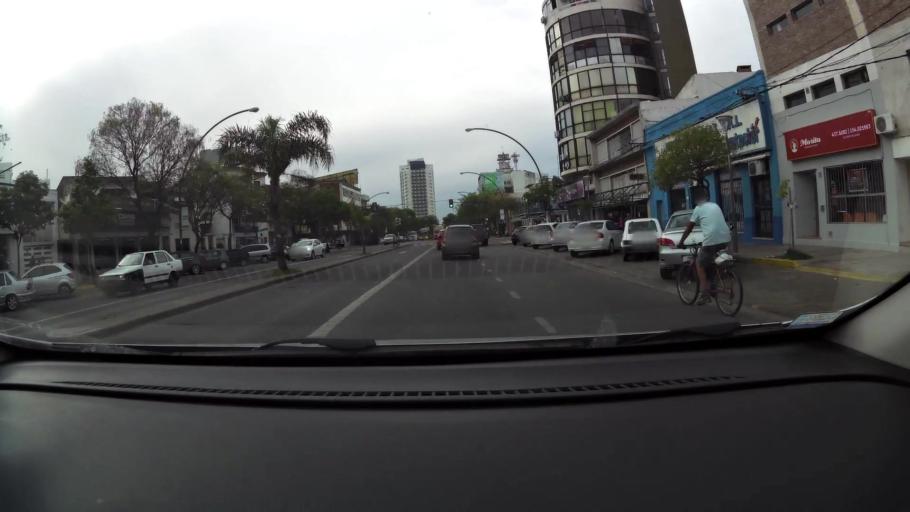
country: AR
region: Santa Fe
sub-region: Departamento de Rosario
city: Rosario
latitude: -32.9167
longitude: -60.6844
